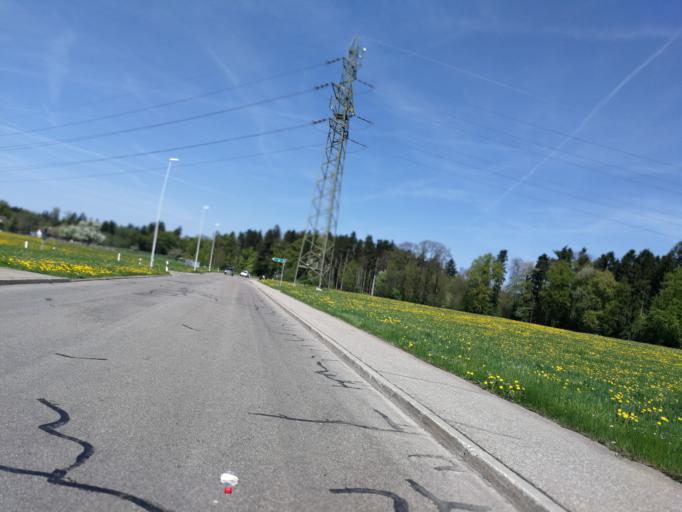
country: CH
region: Zurich
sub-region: Bezirk Hinwil
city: Durnten
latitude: 47.2882
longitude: 8.8232
